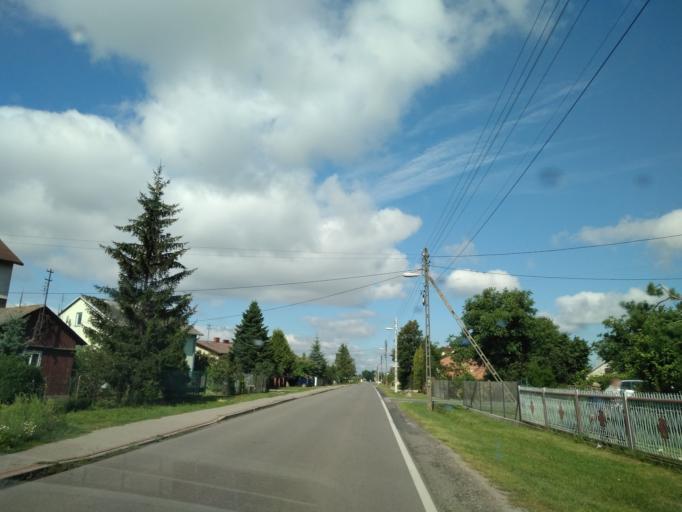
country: PL
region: Lodz Voivodeship
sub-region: Powiat skierniewicki
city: Makow
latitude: 51.9707
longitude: 20.0961
